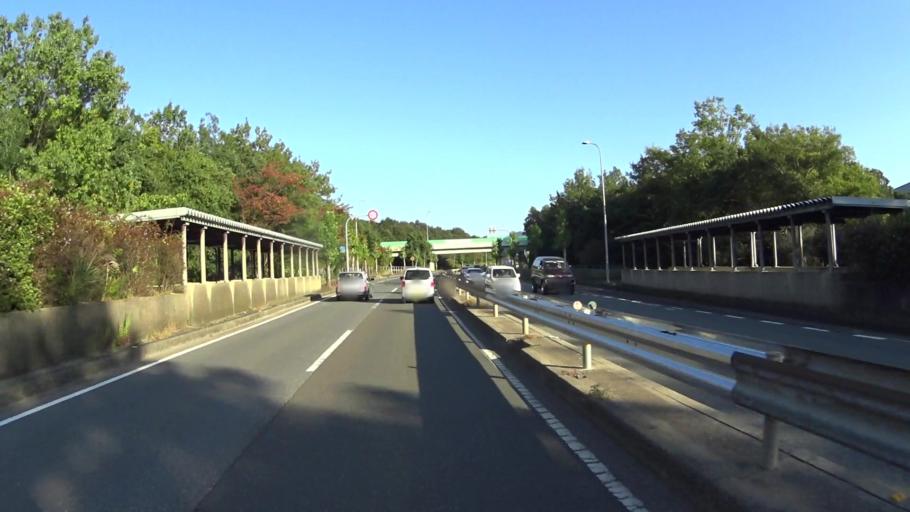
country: JP
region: Kyoto
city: Fukuchiyama
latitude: 35.2867
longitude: 135.1781
